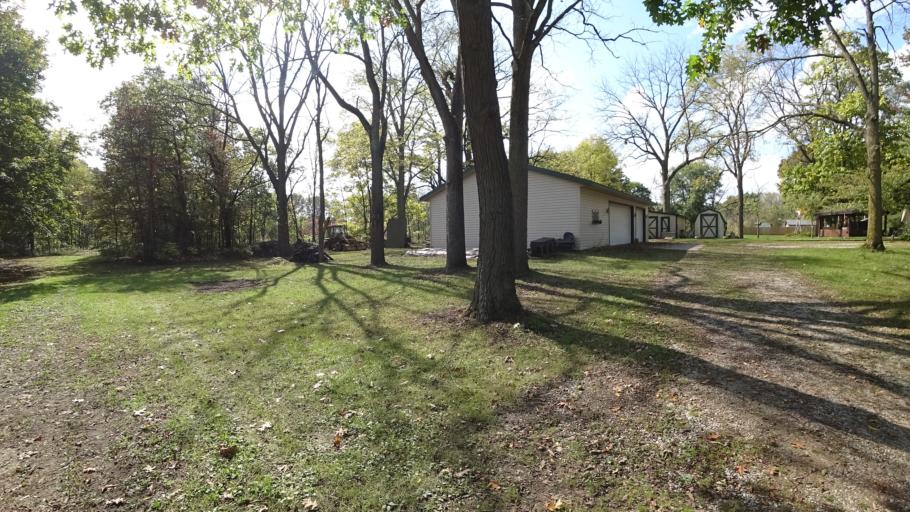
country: US
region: Michigan
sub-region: Saint Joseph County
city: Three Rivers
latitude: 41.9269
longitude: -85.6278
